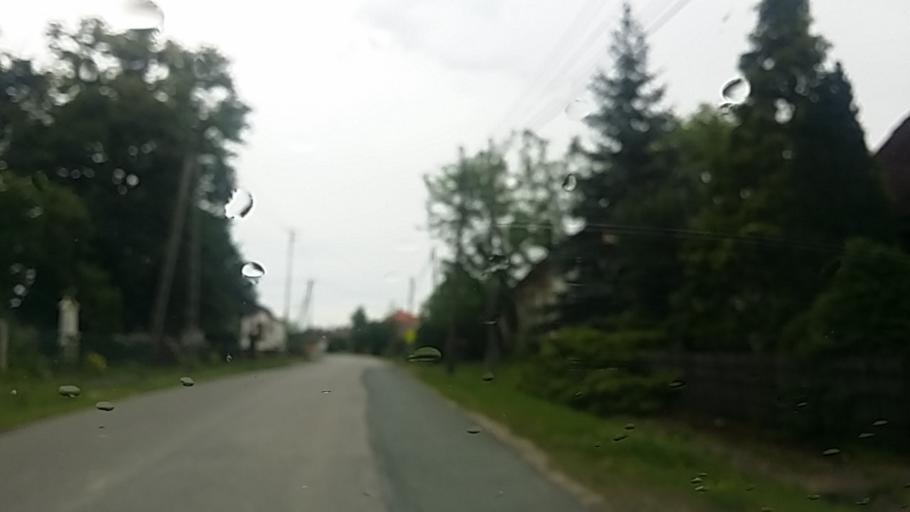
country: HU
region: Zala
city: Zalalovo
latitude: 46.8571
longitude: 16.5013
